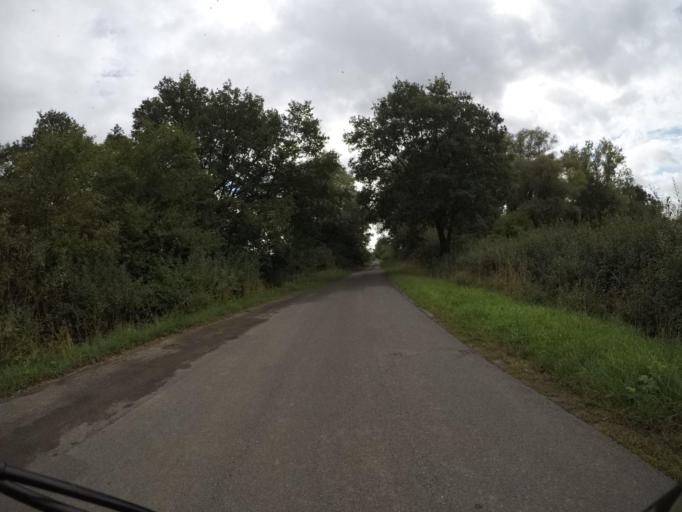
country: DE
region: Lower Saxony
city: Tosterglope
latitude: 53.2692
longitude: 10.8366
